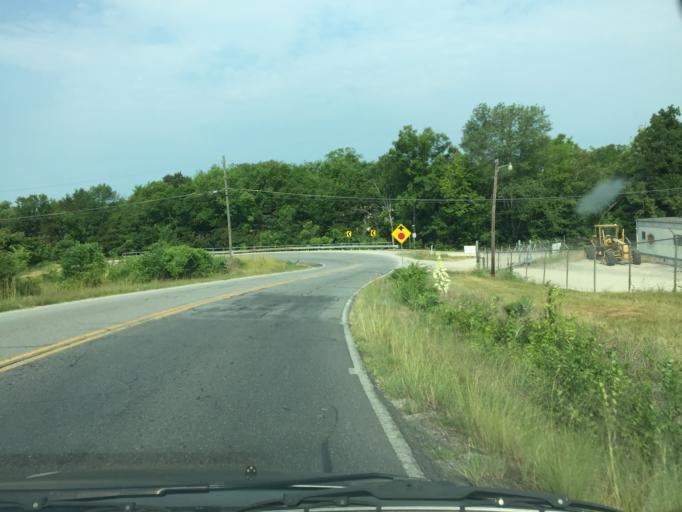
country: US
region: Georgia
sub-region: Catoosa County
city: Ringgold
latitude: 34.9185
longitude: -85.1054
